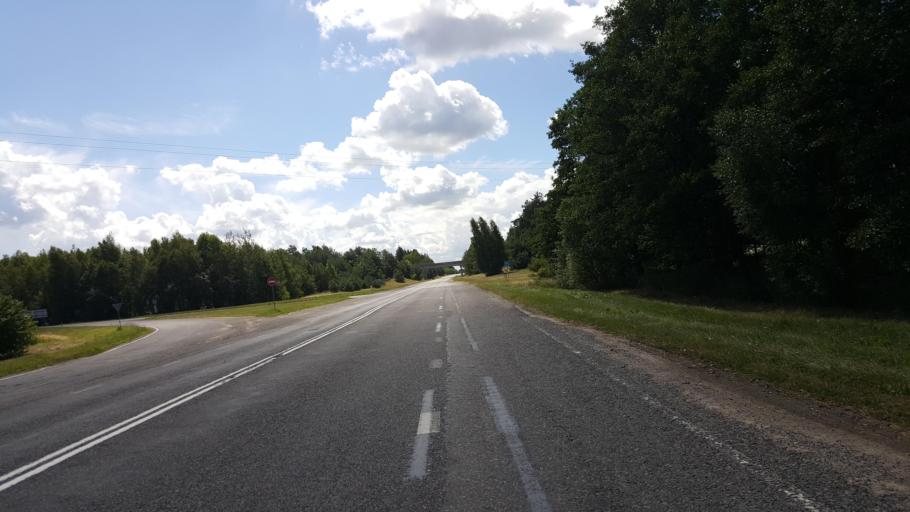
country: BY
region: Brest
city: Kamyanyets
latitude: 52.3448
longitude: 23.9043
